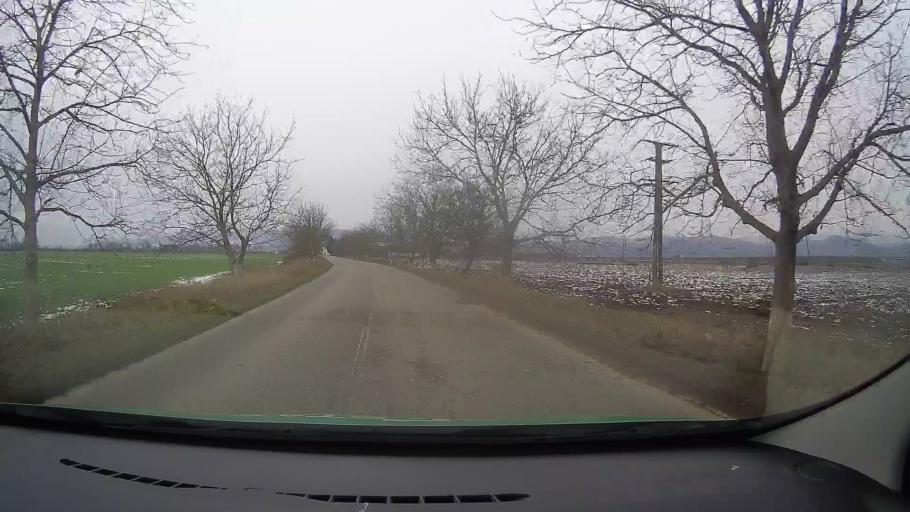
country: RO
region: Hunedoara
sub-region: Comuna Romos
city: Romos
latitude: 45.8820
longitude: 23.2547
